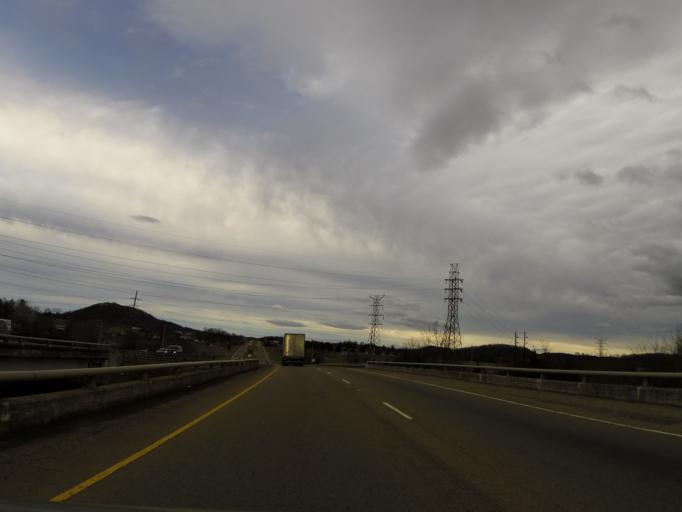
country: US
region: Tennessee
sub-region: Greene County
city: Tusculum
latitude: 36.1938
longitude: -82.7257
